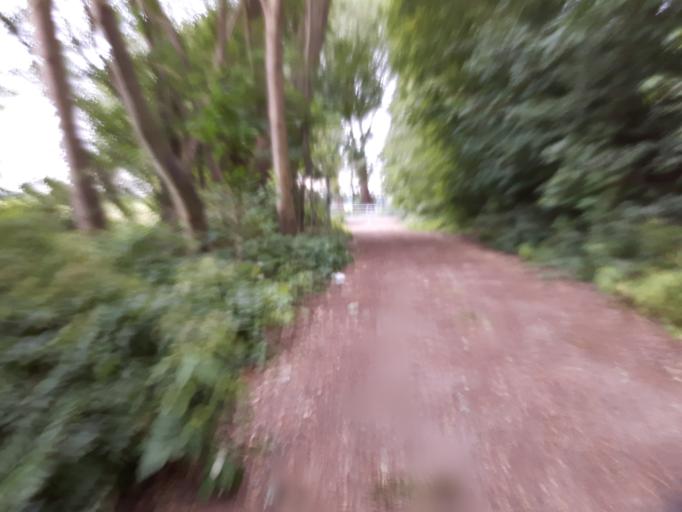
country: DE
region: Hamburg
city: Harburg
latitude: 53.4424
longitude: 10.0130
